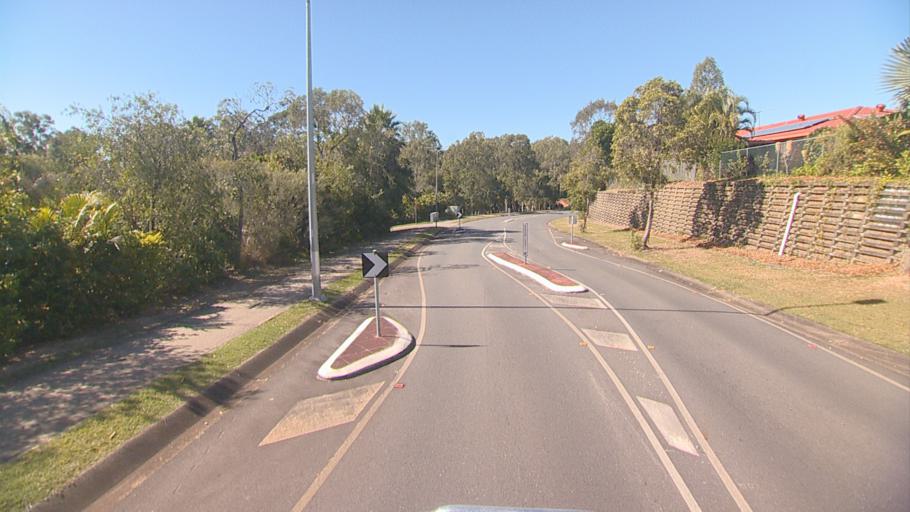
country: AU
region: Queensland
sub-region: Logan
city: Springwood
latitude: -27.6087
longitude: 153.1398
